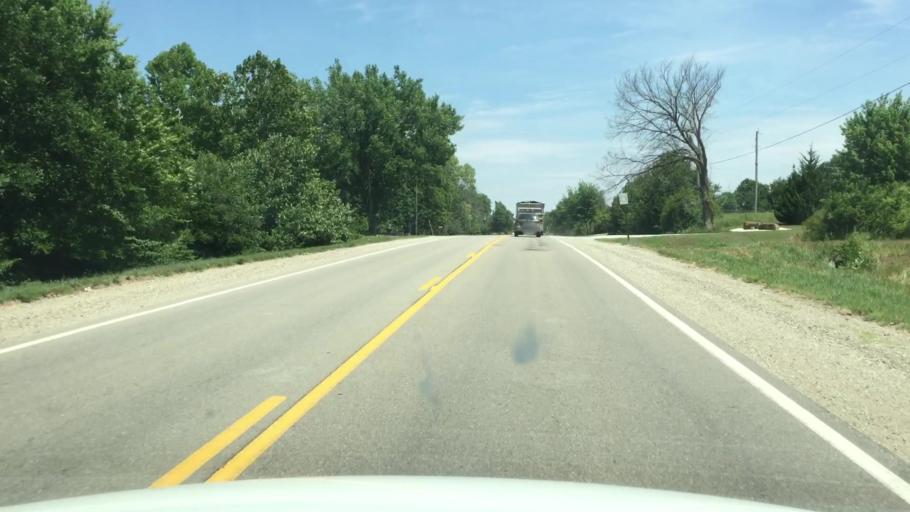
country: US
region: Kansas
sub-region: Shawnee County
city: Topeka
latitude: 38.9861
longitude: -95.5743
